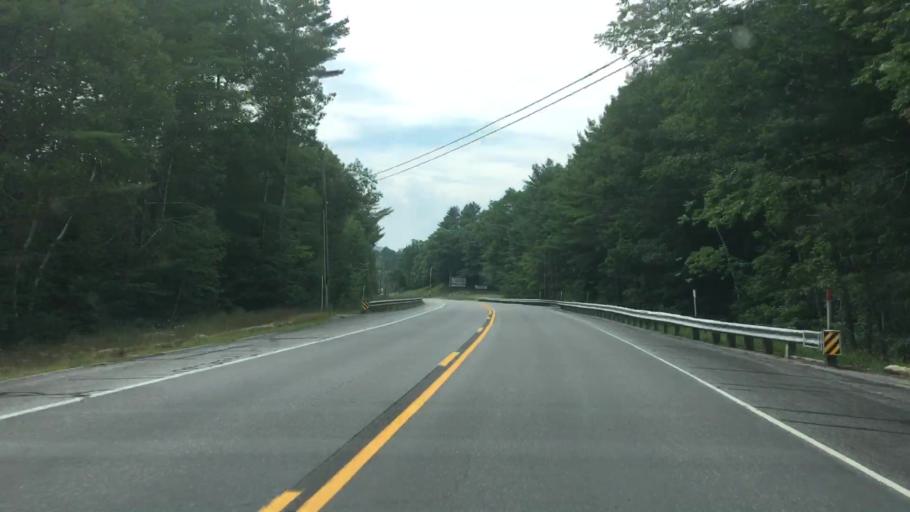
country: US
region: Maine
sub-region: Oxford County
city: Bethel
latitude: 44.4879
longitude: -70.7698
